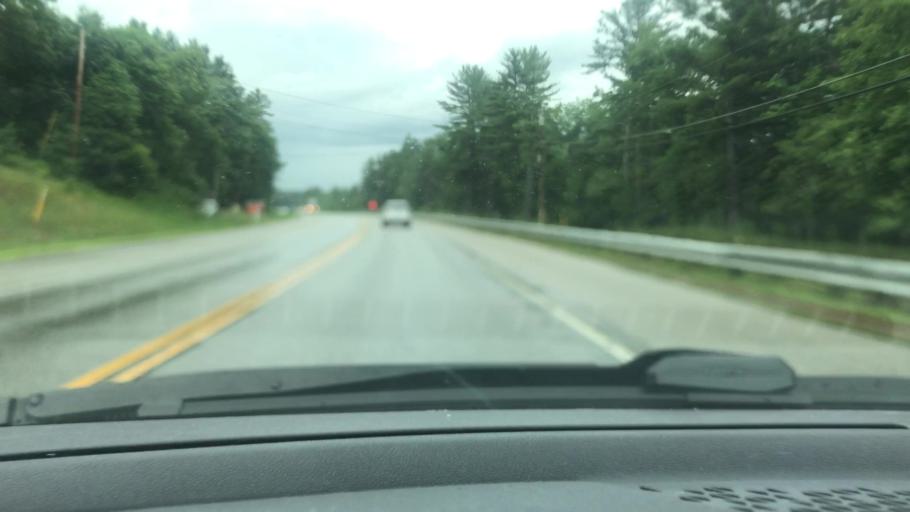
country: US
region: New Hampshire
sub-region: Merrimack County
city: Chichester
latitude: 43.2638
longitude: -71.4576
